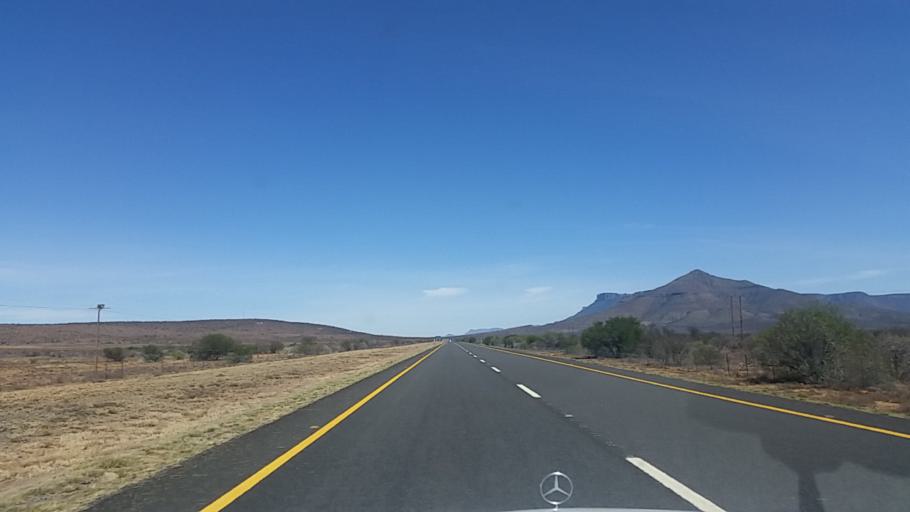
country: ZA
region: Eastern Cape
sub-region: Cacadu District Municipality
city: Graaff-Reinet
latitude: -32.3501
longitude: 24.3326
